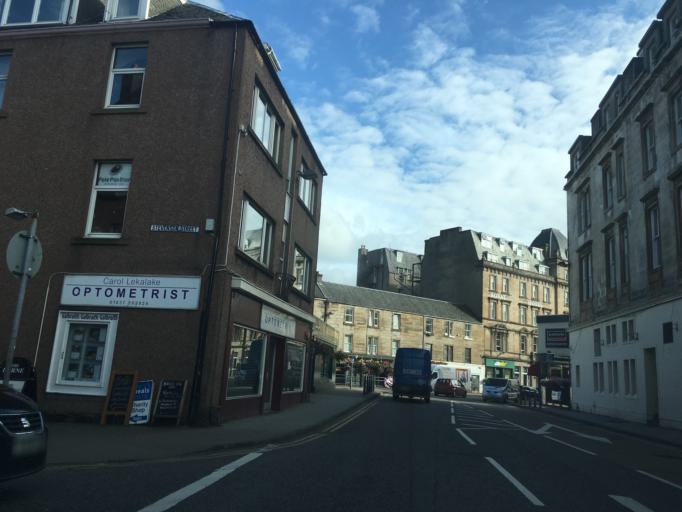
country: GB
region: Scotland
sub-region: Argyll and Bute
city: Oban
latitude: 56.4131
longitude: -5.4721
